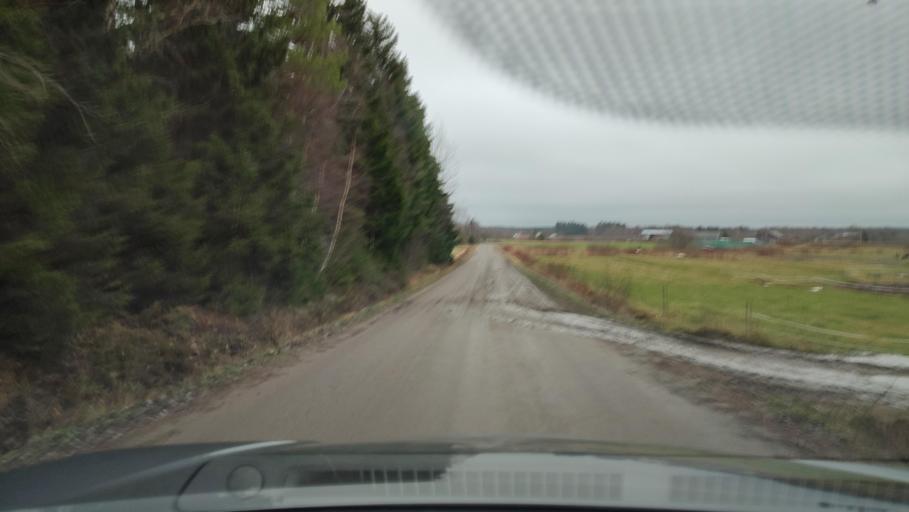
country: FI
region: Southern Ostrobothnia
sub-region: Suupohja
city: Isojoki
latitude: 62.1922
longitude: 21.9501
